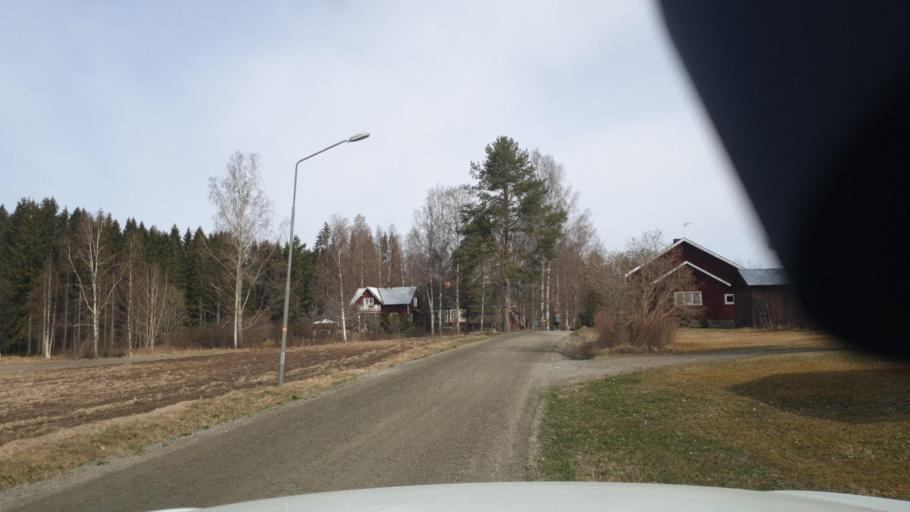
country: SE
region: Vaermland
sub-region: Karlstads Kommun
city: Edsvalla
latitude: 59.6160
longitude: 13.0673
